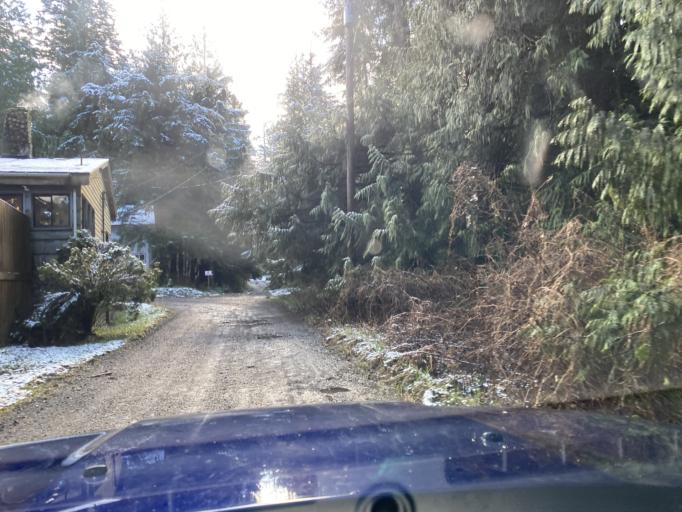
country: US
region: Washington
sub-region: King County
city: Snoqualmie
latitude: 47.5066
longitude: -121.8727
